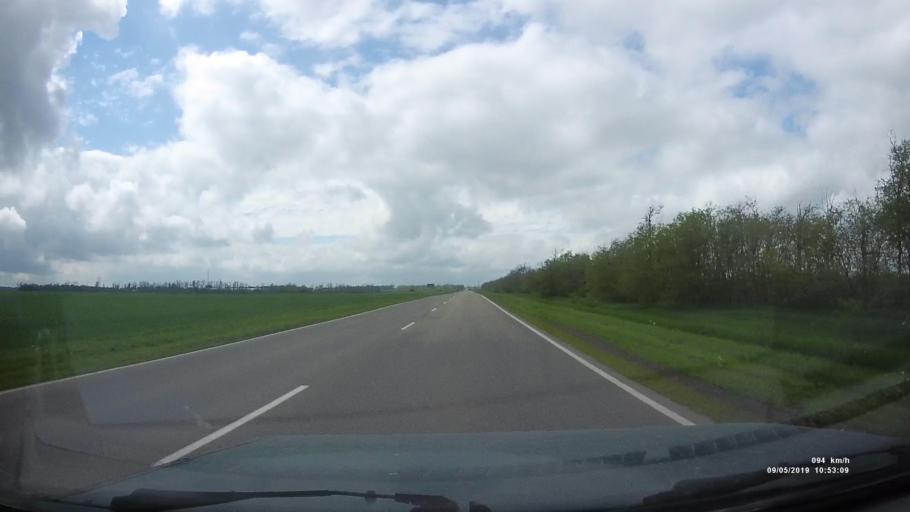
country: RU
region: Rostov
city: Peshkovo
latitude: 46.8925
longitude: 39.3448
